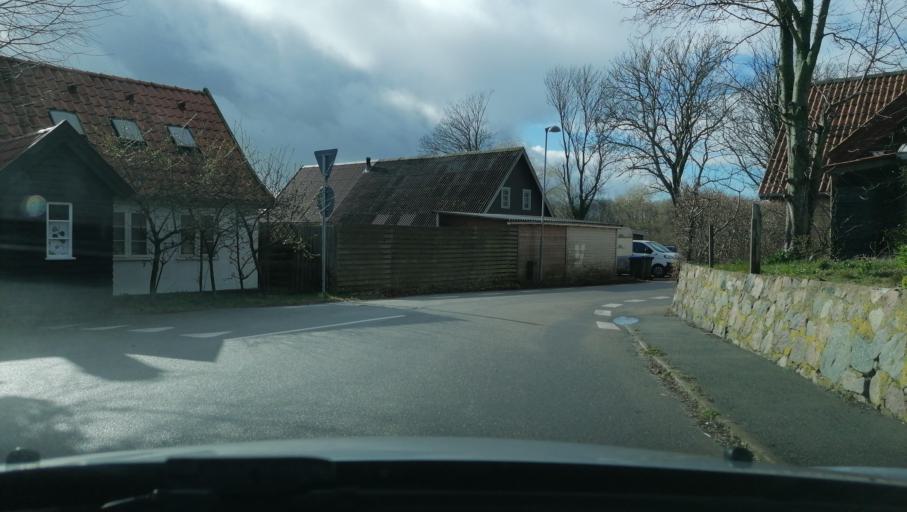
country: DK
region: Zealand
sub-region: Odsherred Kommune
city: Horve
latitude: 55.7397
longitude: 11.3999
